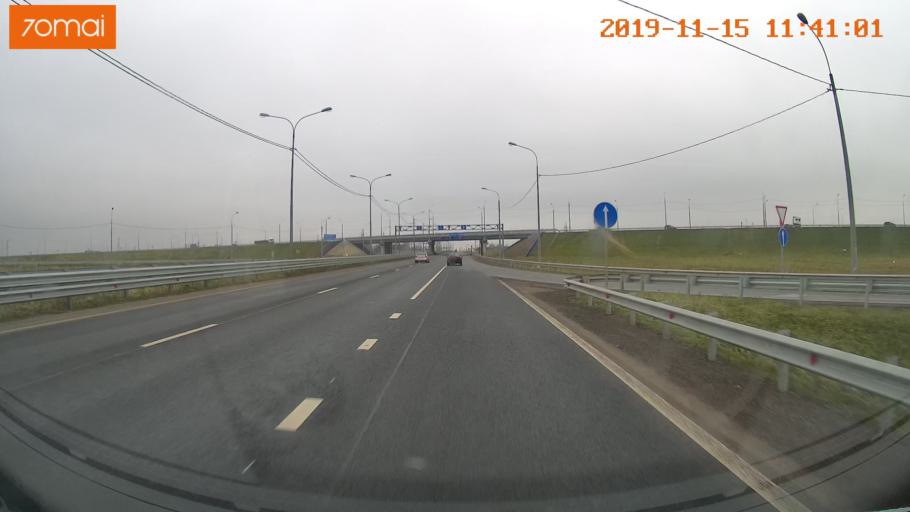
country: RU
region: Vologda
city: Molochnoye
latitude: 59.2130
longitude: 39.7620
